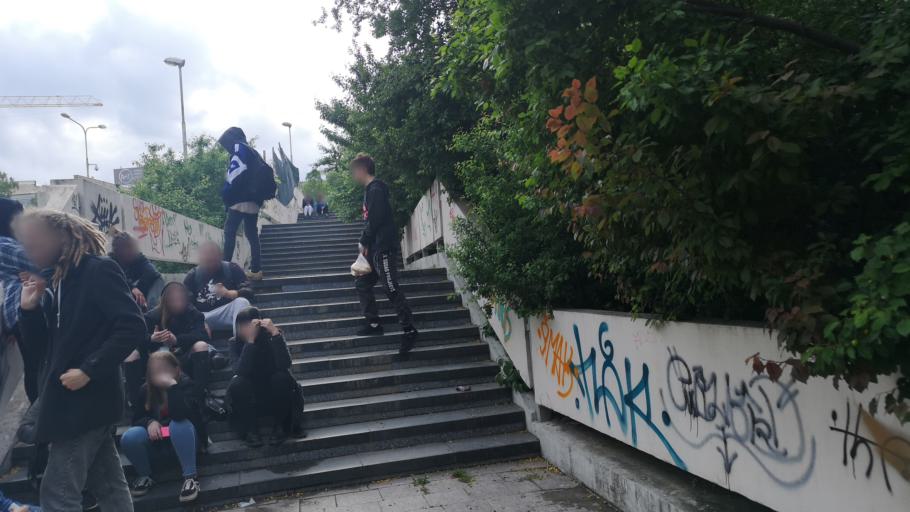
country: SK
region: Nitriansky
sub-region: Okres Nitra
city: Nitra
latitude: 48.3101
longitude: 18.0851
